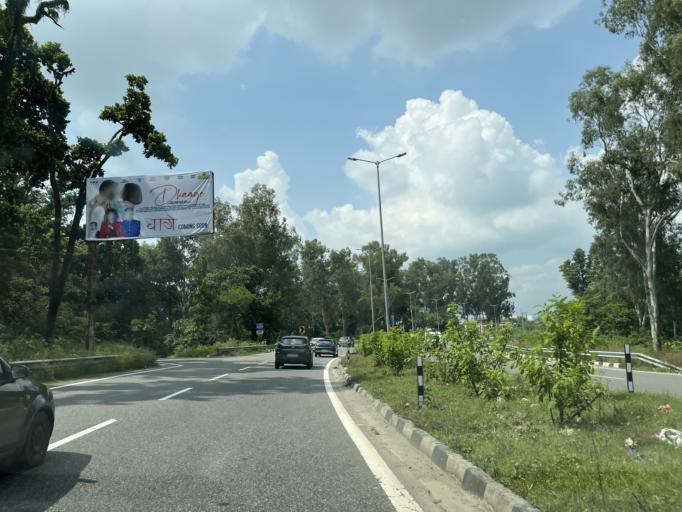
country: IN
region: Uttarakhand
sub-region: Dehradun
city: Raipur
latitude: 30.2503
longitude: 78.0937
